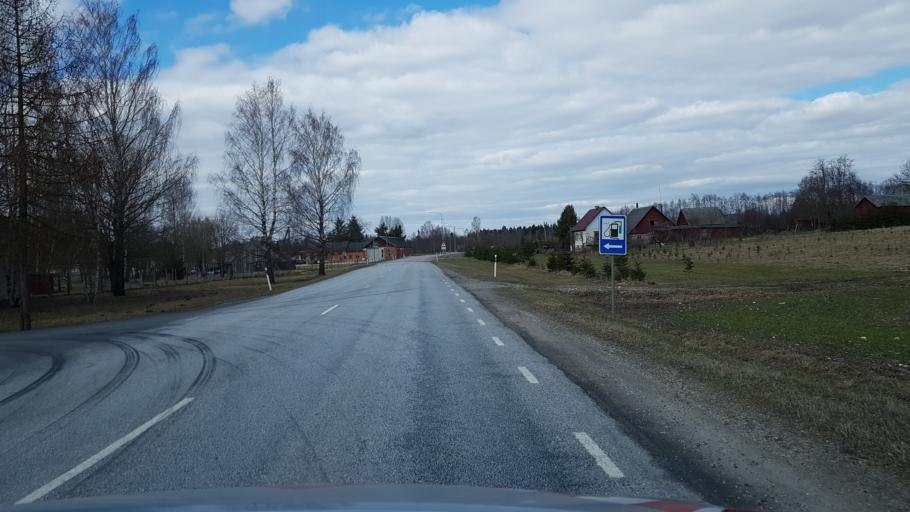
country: EE
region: Laeaene-Virumaa
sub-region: Rakke vald
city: Rakke
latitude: 58.9833
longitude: 26.2640
